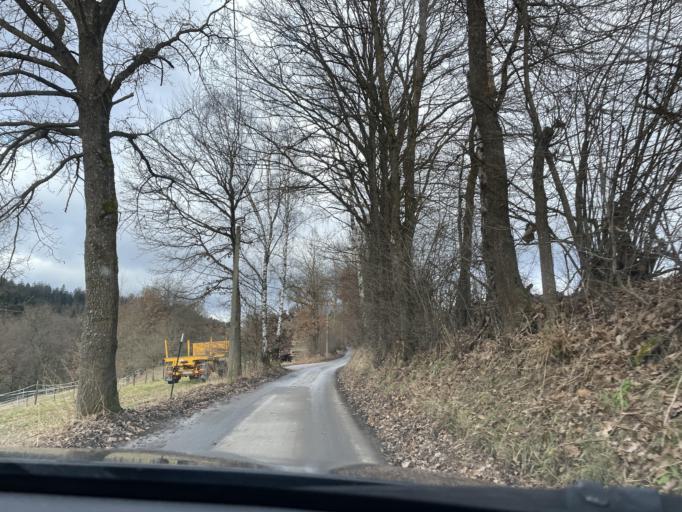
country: DE
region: Bavaria
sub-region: Upper Palatinate
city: Blaibach
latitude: 49.1360
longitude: 12.8332
